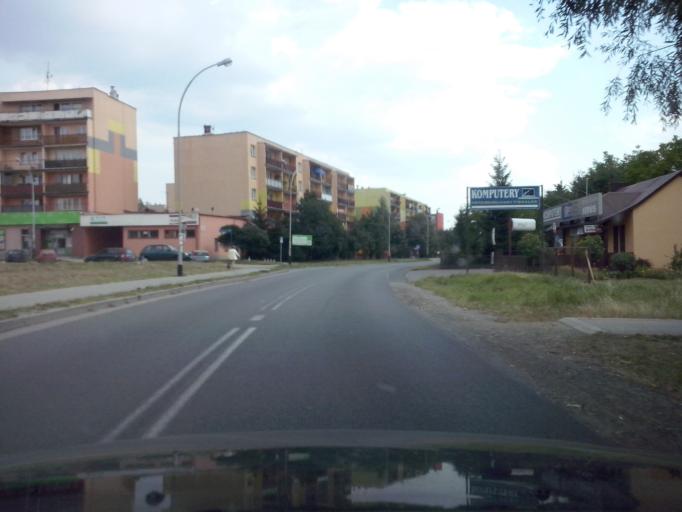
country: PL
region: Subcarpathian Voivodeship
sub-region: Powiat nizanski
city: Nisko
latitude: 50.5203
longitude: 22.1312
